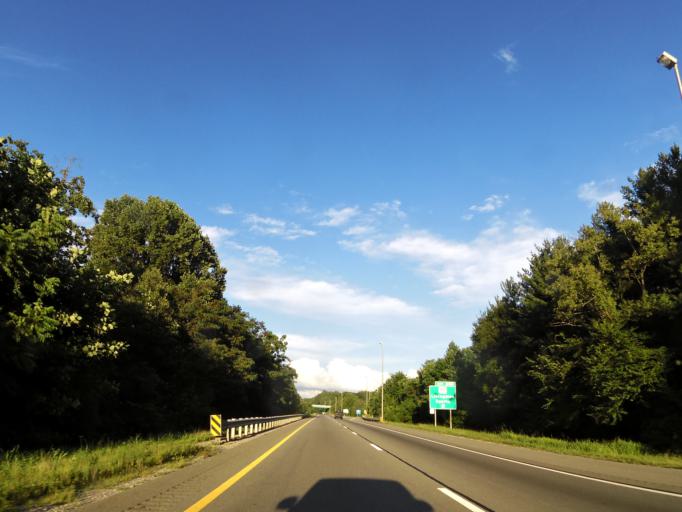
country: US
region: Tennessee
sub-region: Putnam County
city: Cookeville
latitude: 36.1367
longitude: -85.4865
